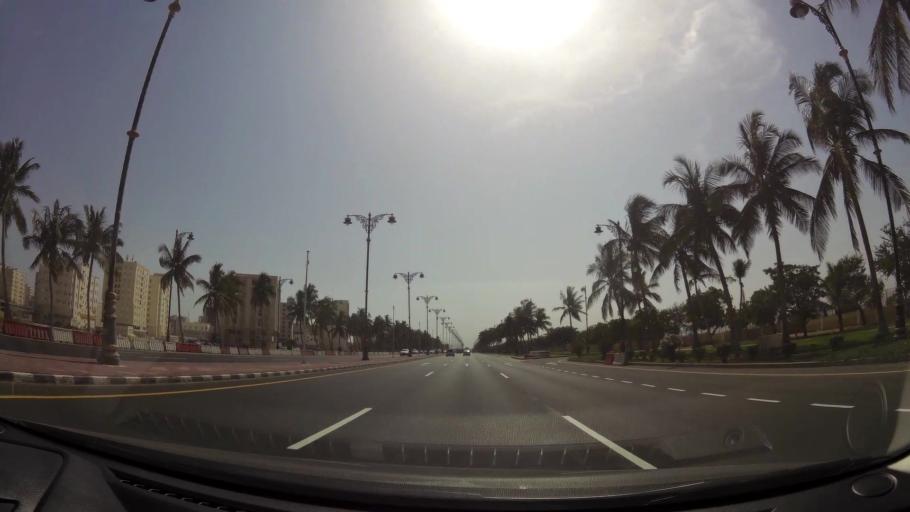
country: OM
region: Zufar
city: Salalah
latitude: 17.0235
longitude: 54.0994
